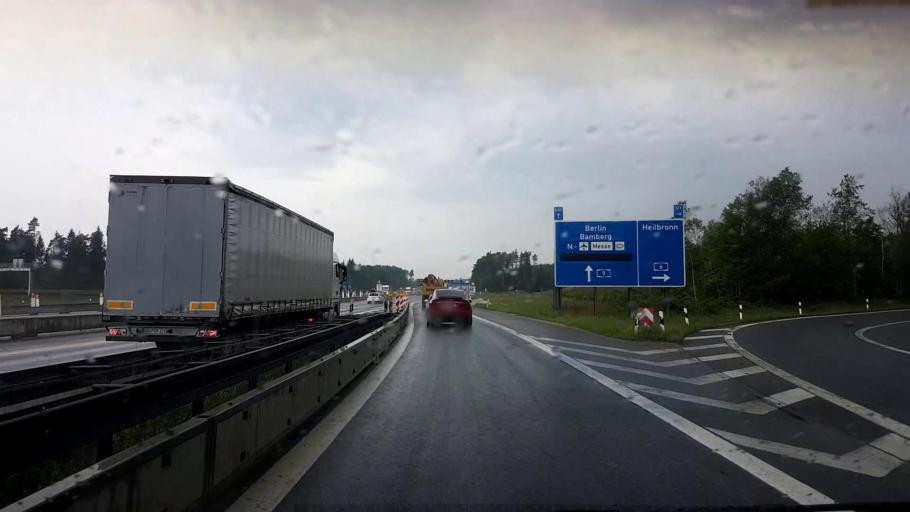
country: DE
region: Bavaria
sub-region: Regierungsbezirk Mittelfranken
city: Feucht
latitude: 49.3965
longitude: 11.2001
